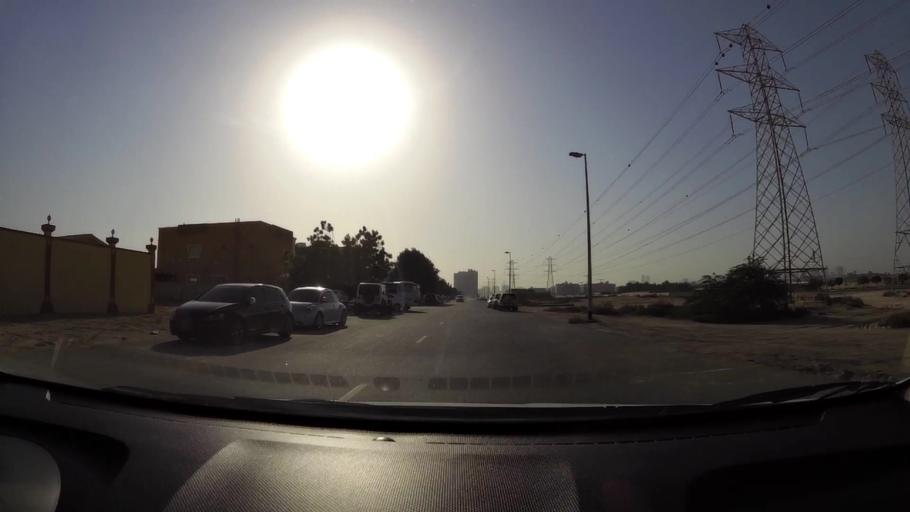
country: AE
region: Ash Shariqah
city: Sharjah
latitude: 25.2714
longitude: 55.3907
